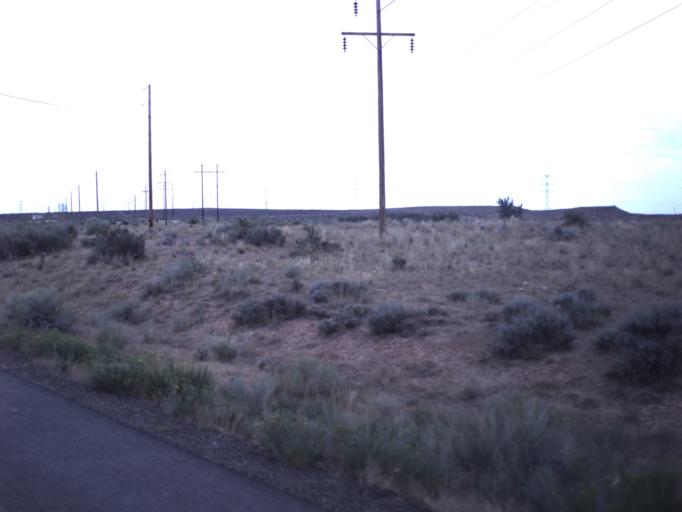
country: US
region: Utah
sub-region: Uintah County
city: Naples
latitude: 40.2218
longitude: -109.3886
